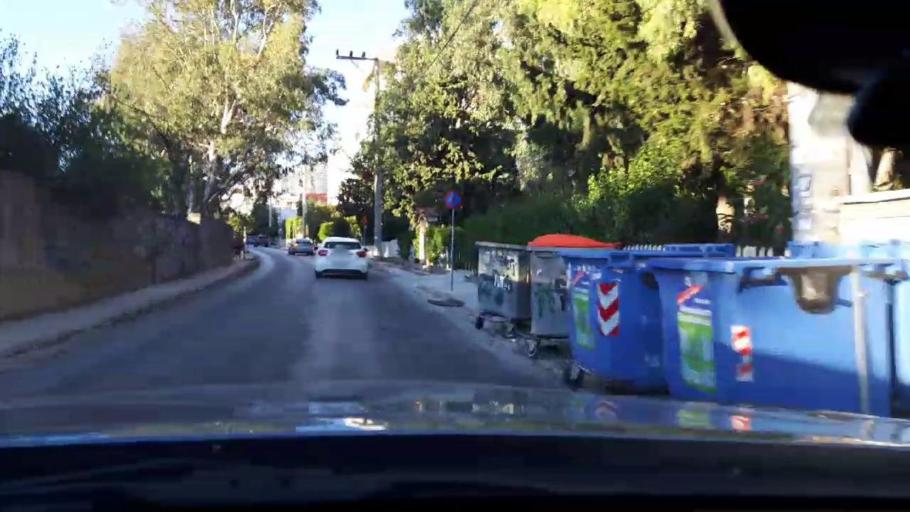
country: GR
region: Attica
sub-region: Nomarchia Athinas
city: Melissia
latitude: 38.0449
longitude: 23.8311
